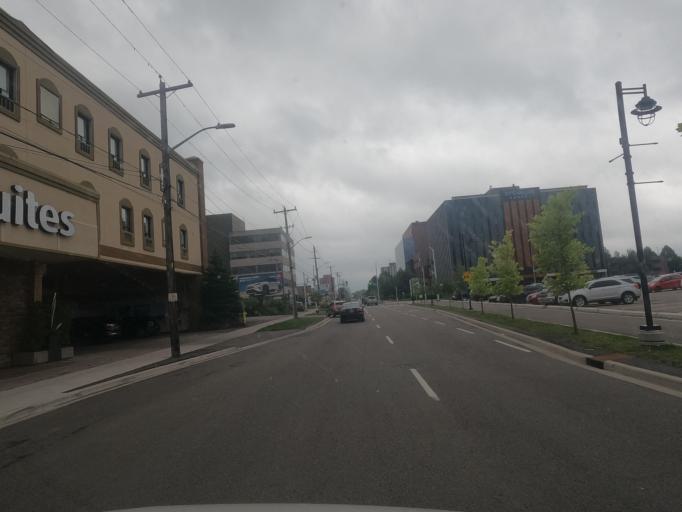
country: CA
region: Ontario
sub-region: Algoma
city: Sault Ste. Marie
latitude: 46.5119
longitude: -84.3360
